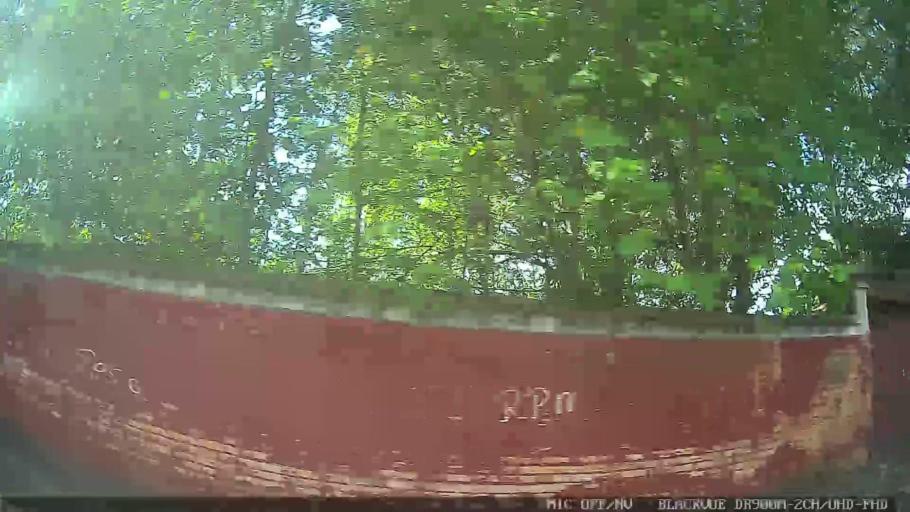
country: BR
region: Sao Paulo
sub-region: Tiete
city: Tiete
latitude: -23.0945
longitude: -47.7080
